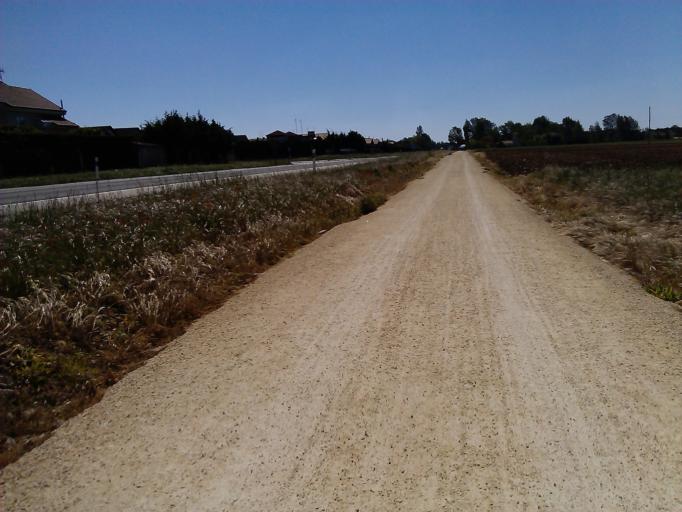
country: ES
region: Castille and Leon
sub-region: Provincia de Burgos
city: Los Tomillares
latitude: 42.3329
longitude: -3.5537
